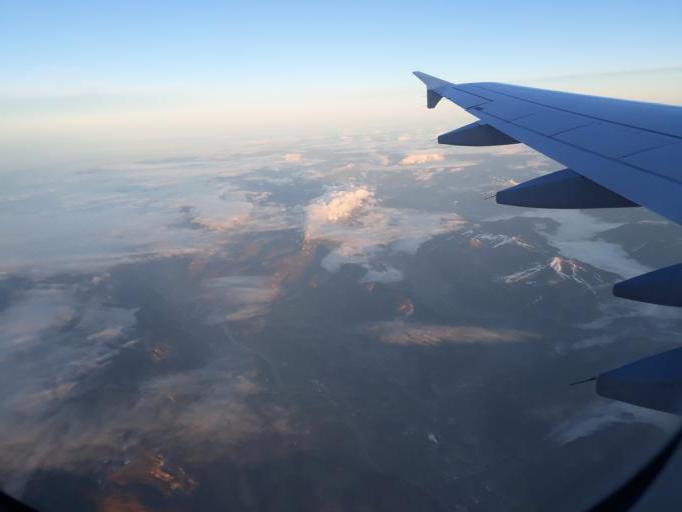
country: AT
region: Tyrol
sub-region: Politischer Bezirk Kufstein
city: Breitenbach am Inn
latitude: 47.4836
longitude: 11.9405
